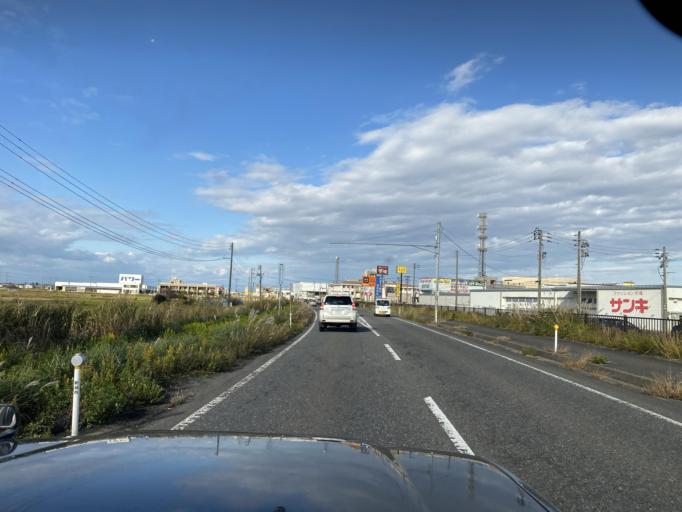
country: JP
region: Niigata
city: Niitsu-honcho
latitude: 37.7843
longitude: 139.1118
